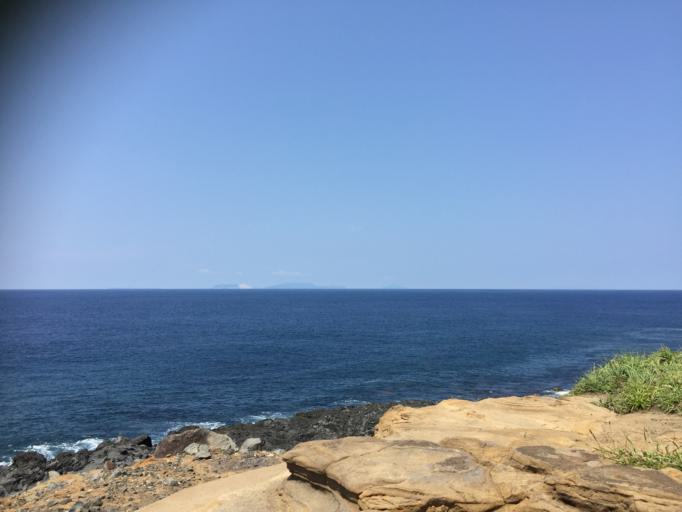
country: JP
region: Shizuoka
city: Shimoda
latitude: 34.1129
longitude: 139.4898
